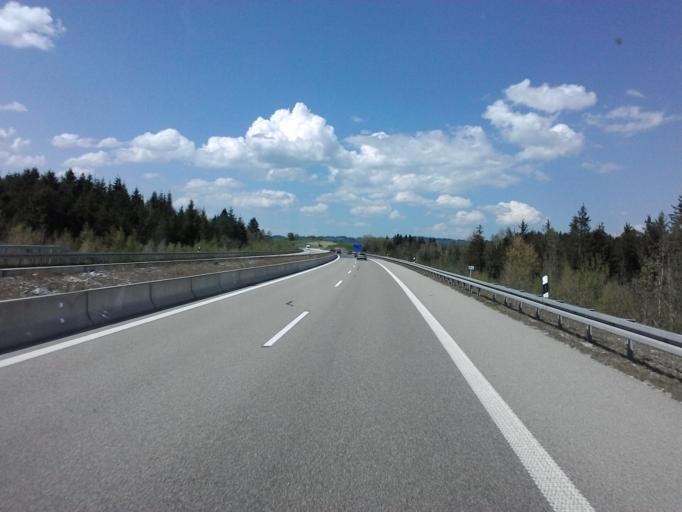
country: DE
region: Bavaria
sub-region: Swabia
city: Fuessen
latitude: 47.5840
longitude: 10.6614
